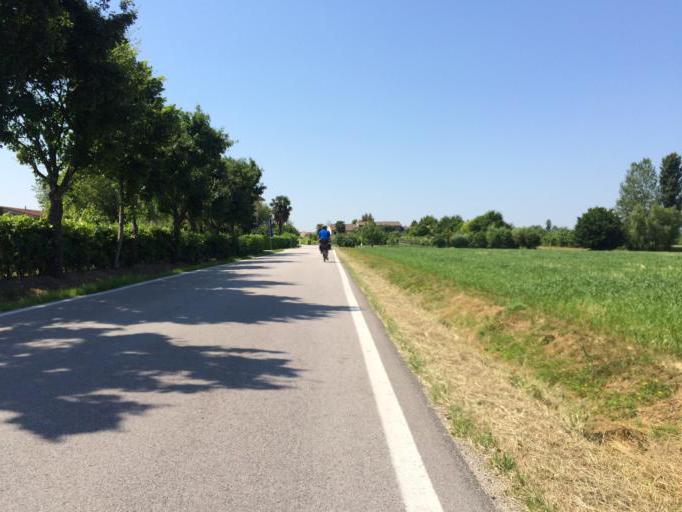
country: IT
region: Veneto
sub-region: Provincia di Vicenza
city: Villaganzerla
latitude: 45.4426
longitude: 11.6302
